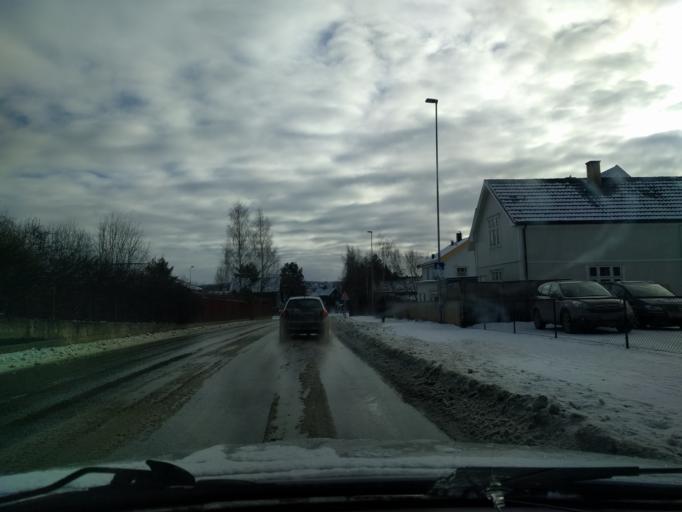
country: NO
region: Hedmark
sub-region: Hamar
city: Hamar
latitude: 60.8000
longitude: 11.0863
